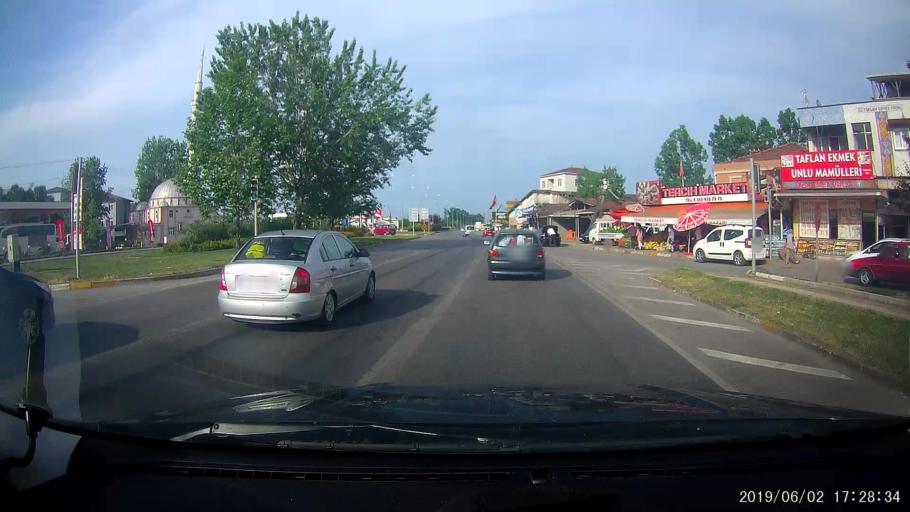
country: TR
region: Samsun
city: Carsamba
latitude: 41.2076
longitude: 36.7468
